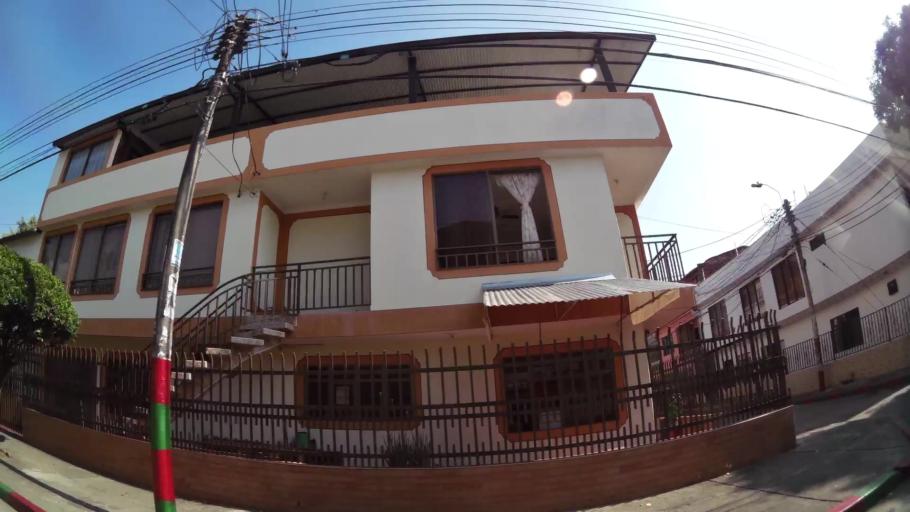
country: CO
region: Valle del Cauca
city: Cali
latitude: 3.4090
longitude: -76.5268
